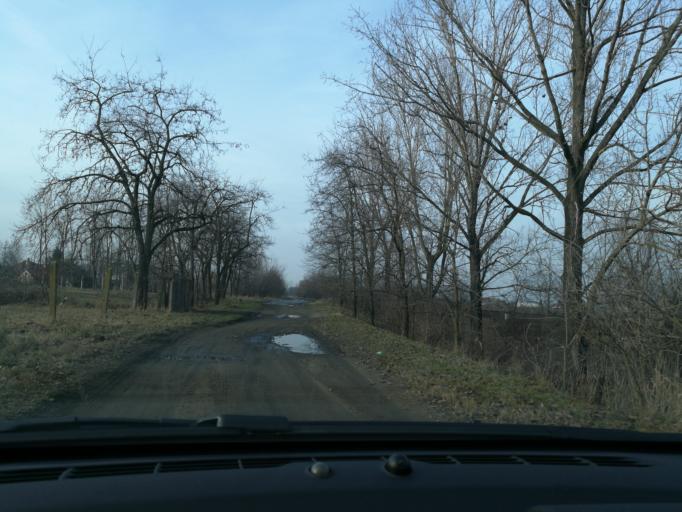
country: HU
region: Szabolcs-Szatmar-Bereg
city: Nyiregyhaza
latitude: 47.9605
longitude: 21.6921
